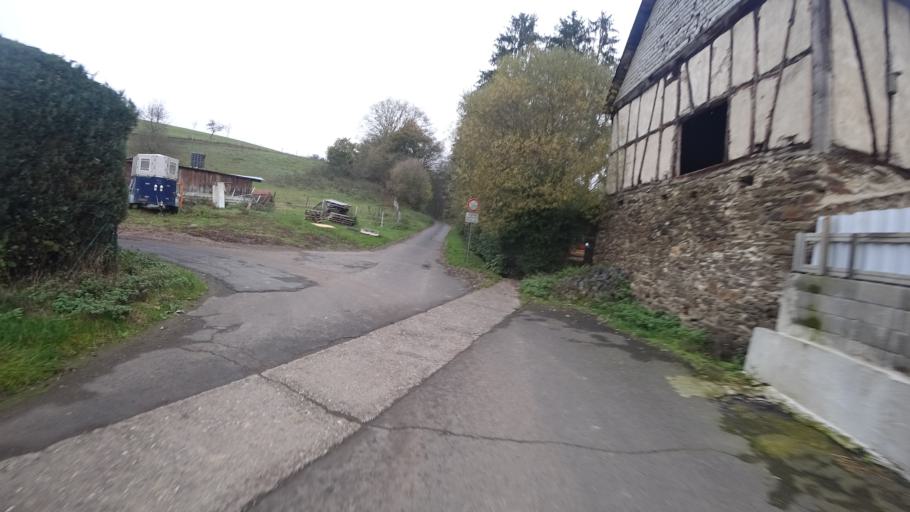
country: DE
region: Rheinland-Pfalz
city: Isselbach
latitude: 50.3909
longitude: 7.8907
